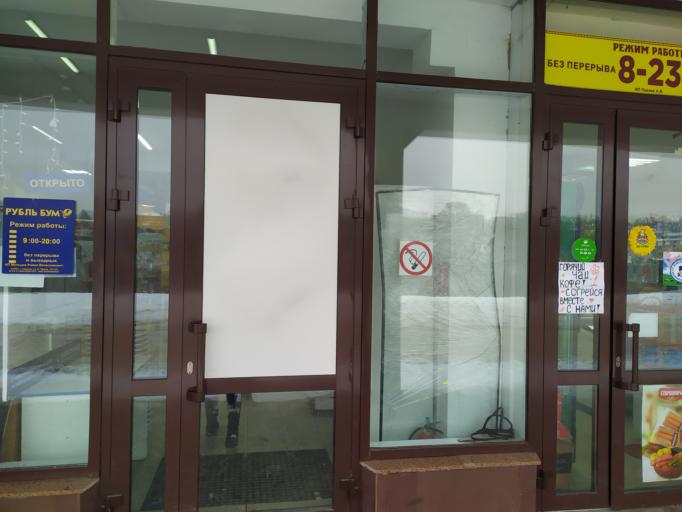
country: RU
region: Chuvashia
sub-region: Cheboksarskiy Rayon
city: Cheboksary
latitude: 56.1196
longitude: 47.2085
